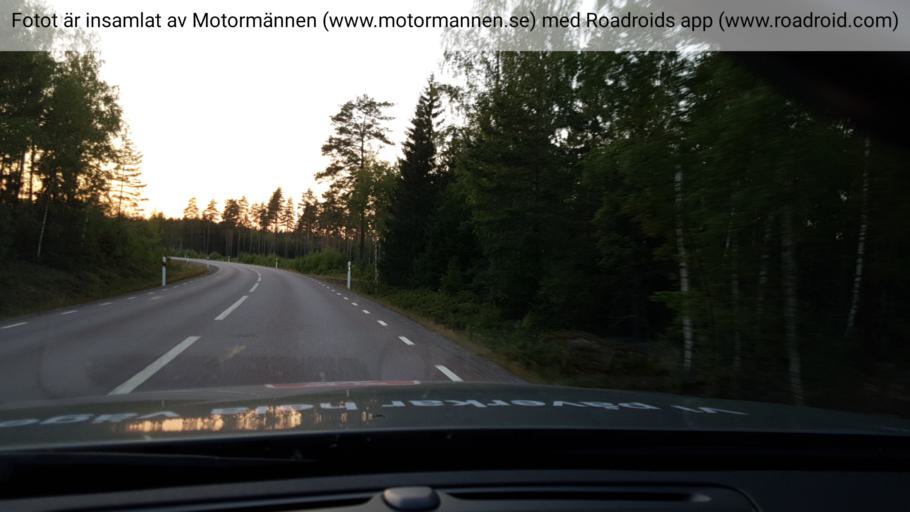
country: SE
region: Uppsala
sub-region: Heby Kommun
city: OEstervala
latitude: 60.0460
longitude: 17.2393
